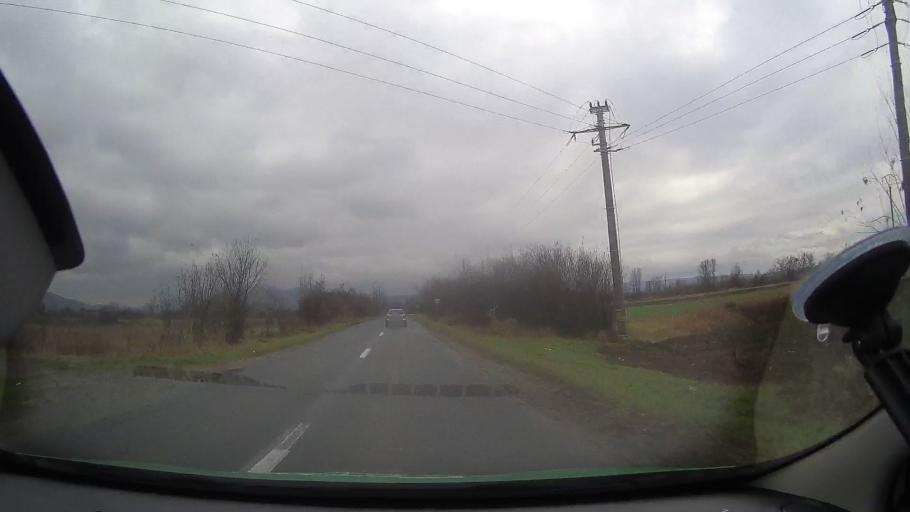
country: RO
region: Arad
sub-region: Comuna Sebis
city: Sebis
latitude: 46.3529
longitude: 22.1304
